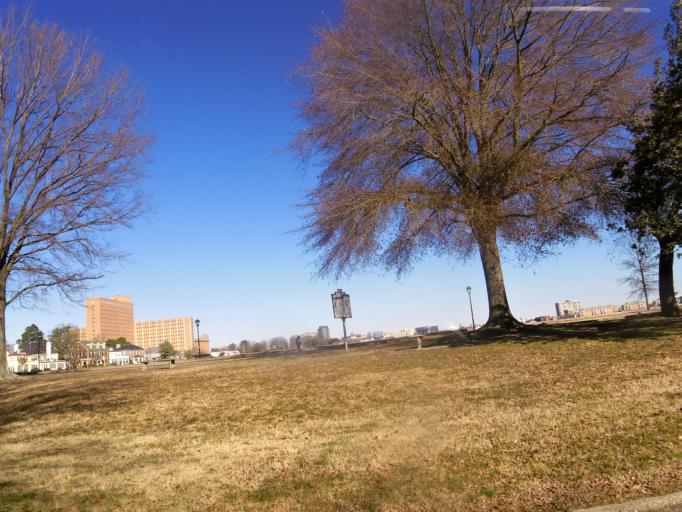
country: US
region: Virginia
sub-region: City of Portsmouth
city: Portsmouth
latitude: 36.8401
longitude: -76.3018
